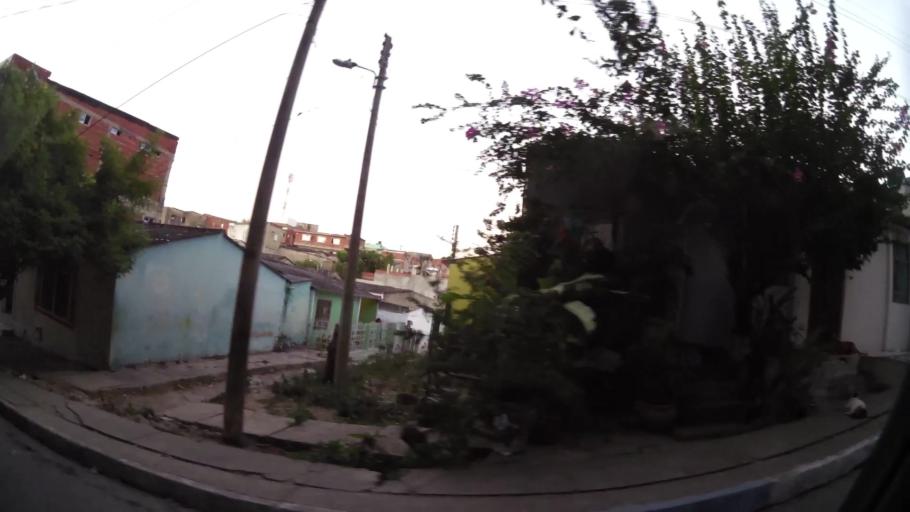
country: CO
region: Bolivar
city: Cartagena
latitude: 10.4008
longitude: -75.5142
